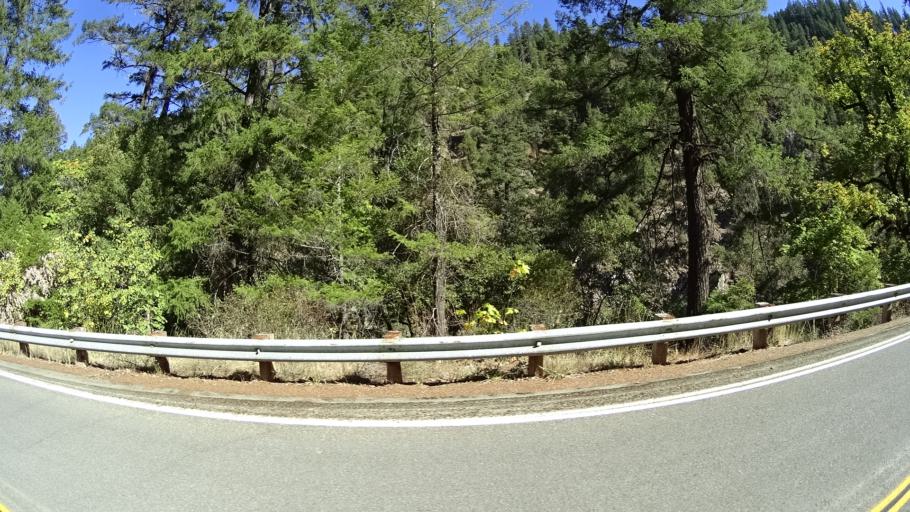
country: US
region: California
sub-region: Siskiyou County
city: Happy Camp
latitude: 41.3563
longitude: -123.4089
